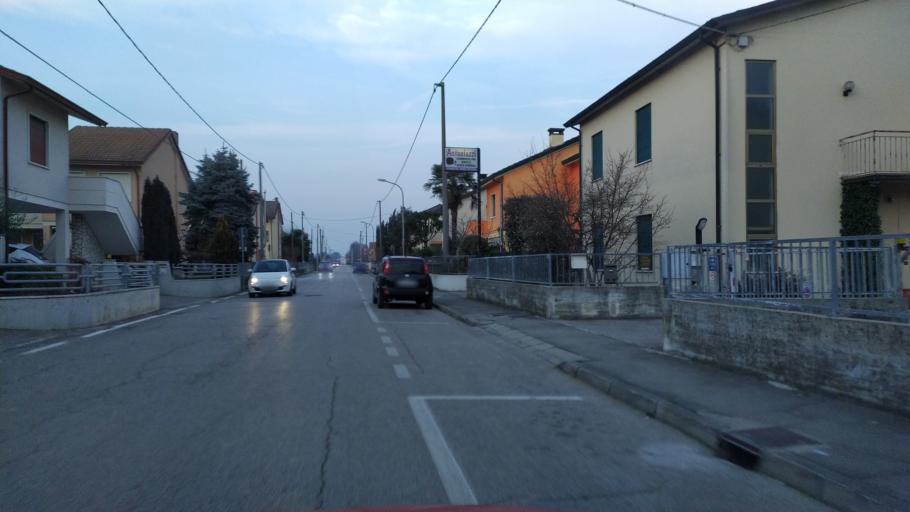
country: IT
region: Veneto
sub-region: Provincia di Vicenza
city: Monticello Conte Otto
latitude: 45.5959
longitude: 11.5806
